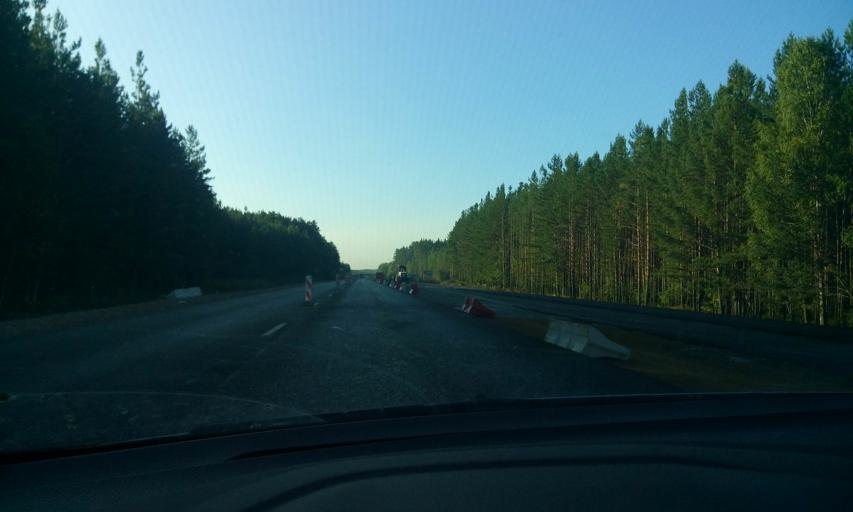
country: RU
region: Sverdlovsk
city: Shchelkun
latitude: 56.2902
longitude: 60.8708
